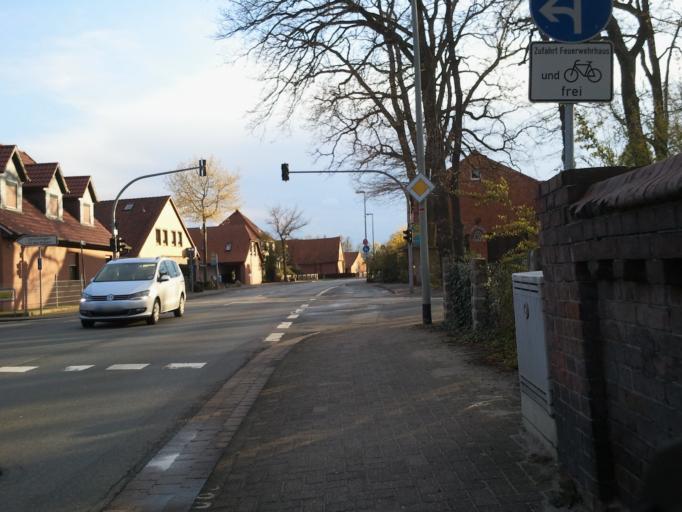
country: DE
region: Lower Saxony
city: Nienburg
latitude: 52.6626
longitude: 9.2437
